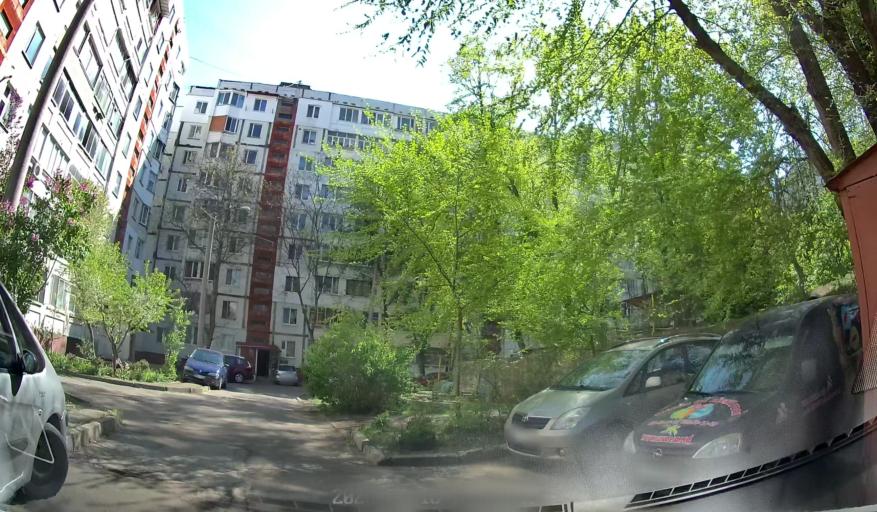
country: MD
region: Chisinau
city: Chisinau
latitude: 47.0449
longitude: 28.8862
